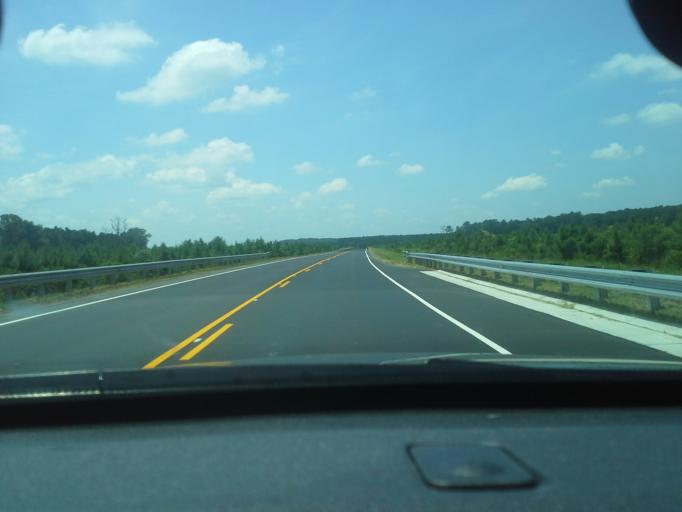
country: US
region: North Carolina
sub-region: Chowan County
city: Edenton
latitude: 35.9273
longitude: -76.5150
